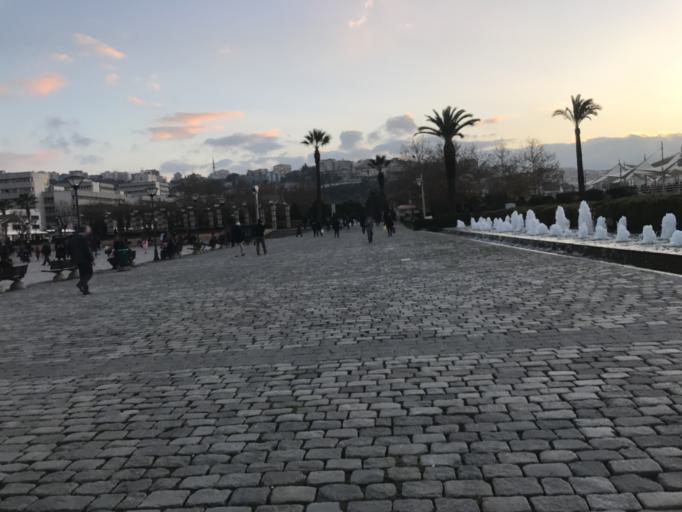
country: TR
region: Izmir
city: Izmir
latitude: 38.4193
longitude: 27.1284
